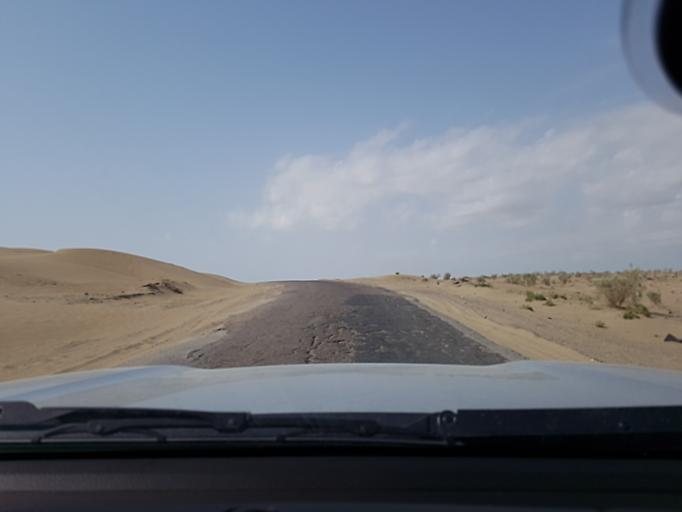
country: TM
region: Balkan
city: Gumdag
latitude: 39.1290
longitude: 54.5781
